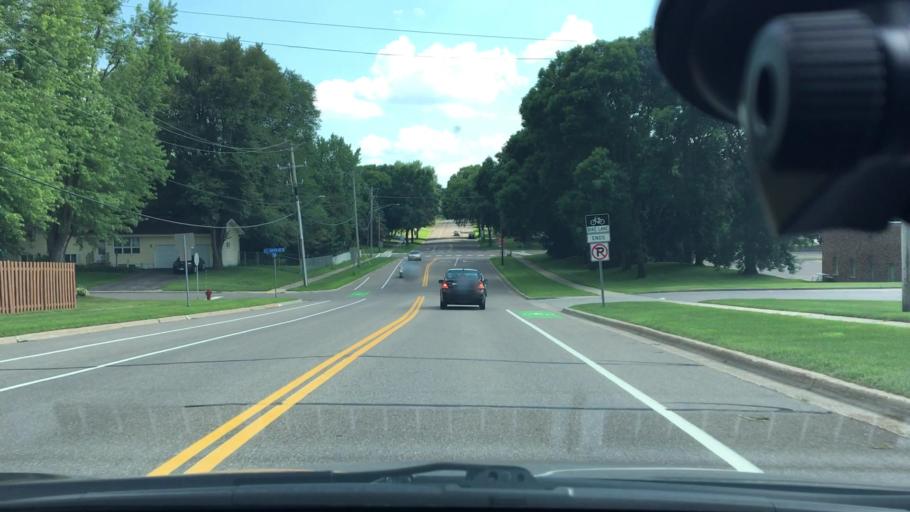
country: US
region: Minnesota
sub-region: Hennepin County
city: New Hope
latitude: 45.0452
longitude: -93.3906
